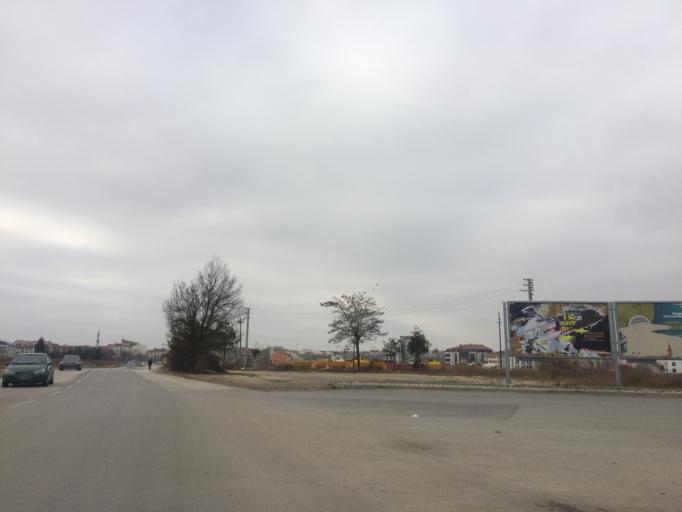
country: TR
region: Eskisehir
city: Eskisehir
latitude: 39.7801
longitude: 30.4954
